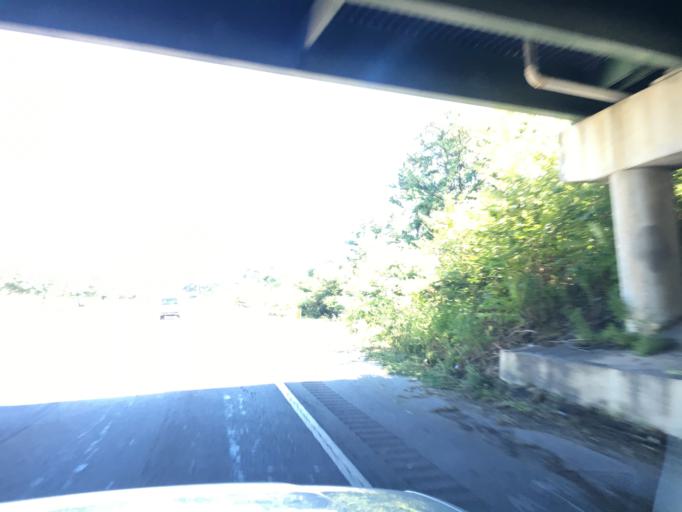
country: US
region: South Carolina
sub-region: Greenville County
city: Mauldin
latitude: 34.8398
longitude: -82.3145
